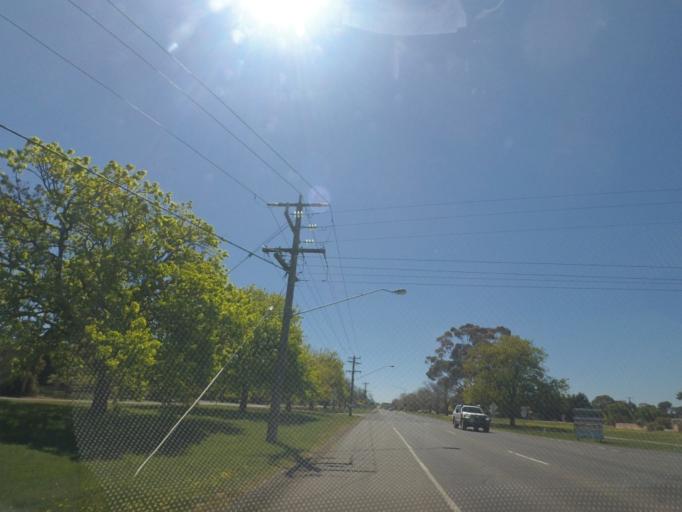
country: AU
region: Victoria
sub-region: Hume
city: Sunbury
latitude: -37.3562
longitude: 144.7436
